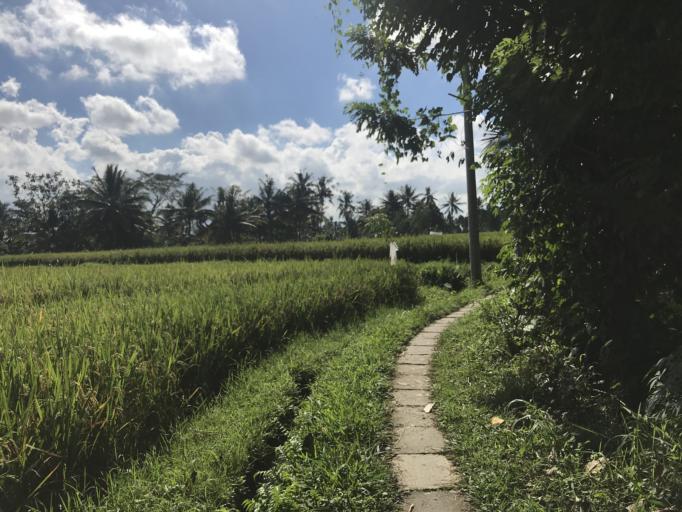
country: ID
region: Bali
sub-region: Kabupaten Gianyar
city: Ubud
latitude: -8.4891
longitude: 115.2617
